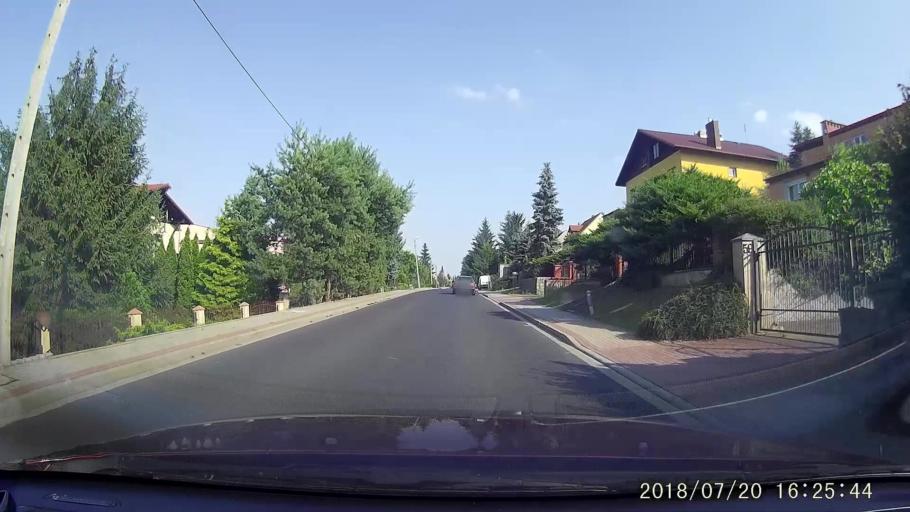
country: PL
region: Lower Silesian Voivodeship
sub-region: Powiat zgorzelecki
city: Zgorzelec
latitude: 51.1328
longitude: 15.0313
